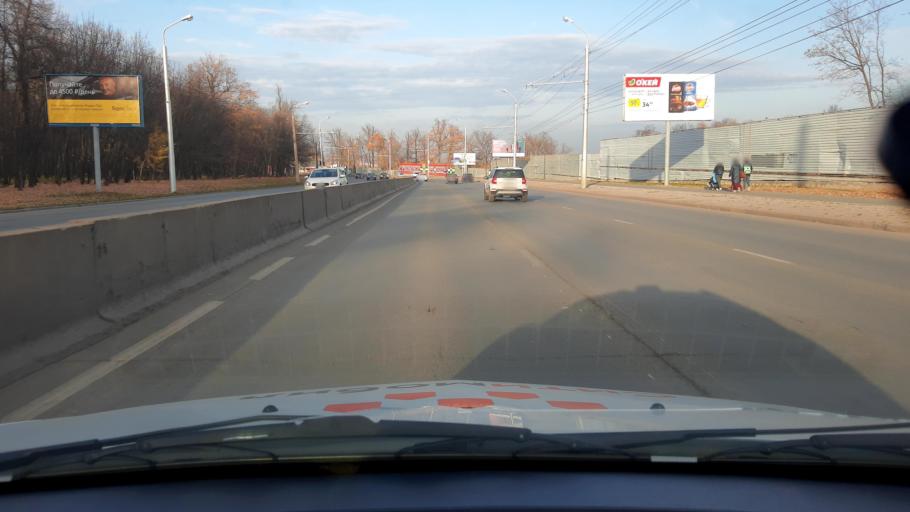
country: RU
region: Bashkortostan
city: Ufa
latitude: 54.7273
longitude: 56.0215
